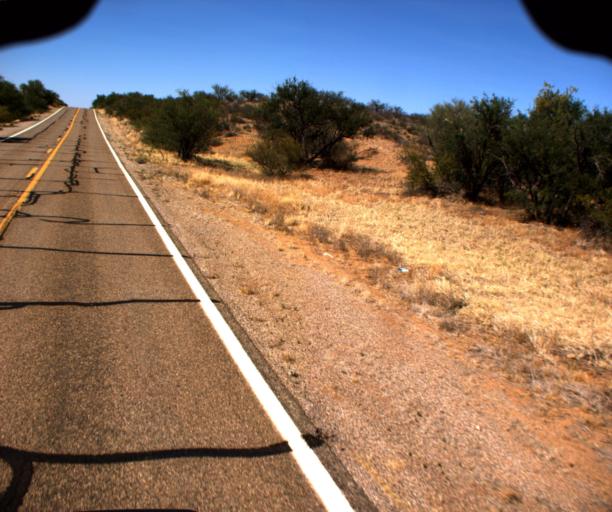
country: US
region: Arizona
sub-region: Pima County
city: Three Points
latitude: 31.8934
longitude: -111.3928
